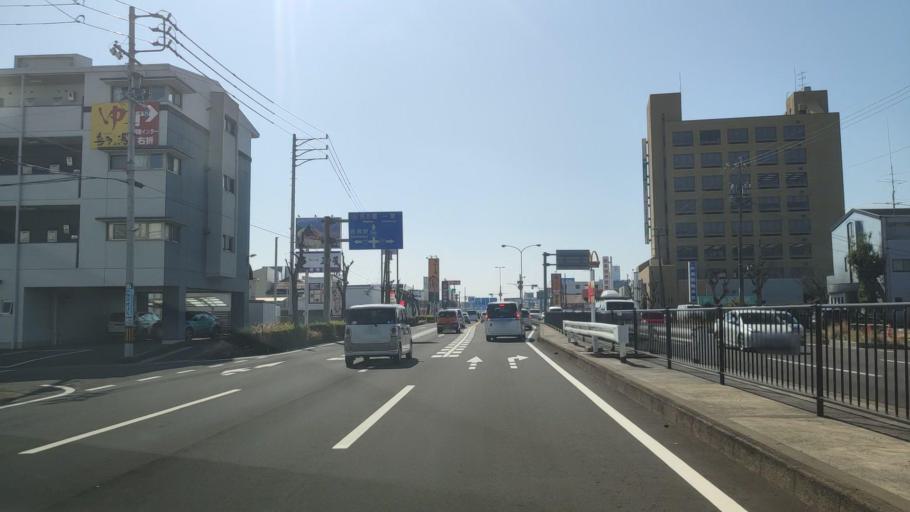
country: JP
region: Gifu
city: Kasamatsucho
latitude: 35.3947
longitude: 136.7852
